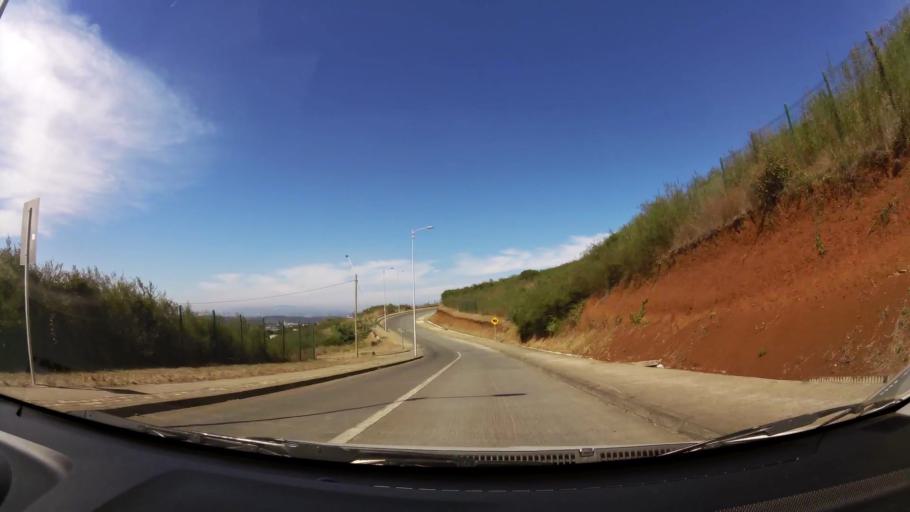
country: CL
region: Biobio
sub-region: Provincia de Concepcion
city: Talcahuano
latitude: -36.7091
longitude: -73.1236
